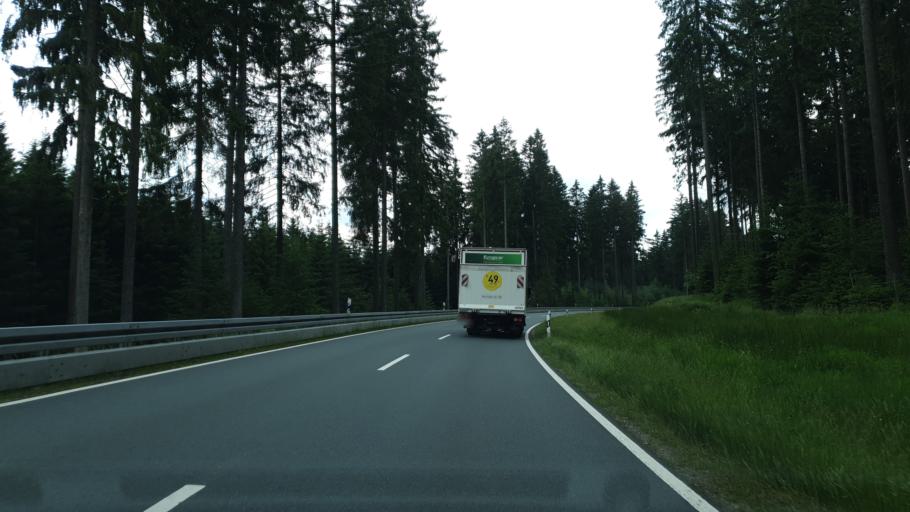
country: DE
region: Saxony
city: Tannenbergsthal
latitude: 50.4593
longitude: 12.4499
